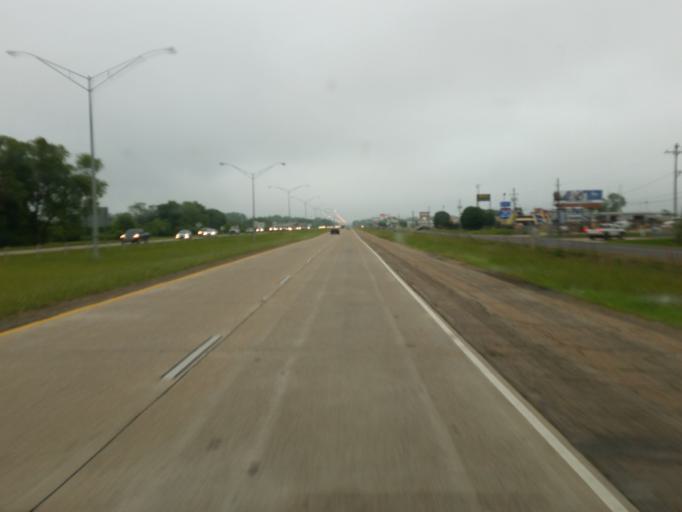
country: US
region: Louisiana
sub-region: Bossier Parish
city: Red Chute
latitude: 32.5305
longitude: -93.6662
